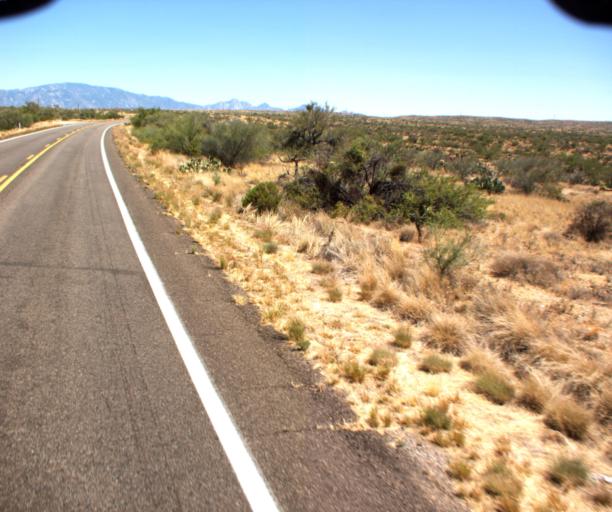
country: US
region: Arizona
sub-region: Pima County
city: Catalina
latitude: 32.6352
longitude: -111.0083
